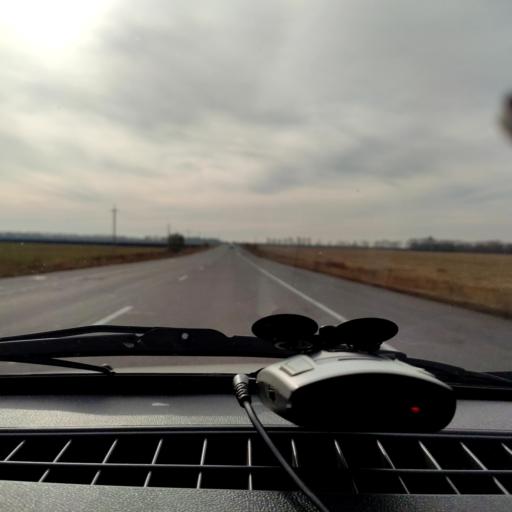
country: RU
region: Voronezj
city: Strelitsa
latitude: 51.5610
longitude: 38.9733
